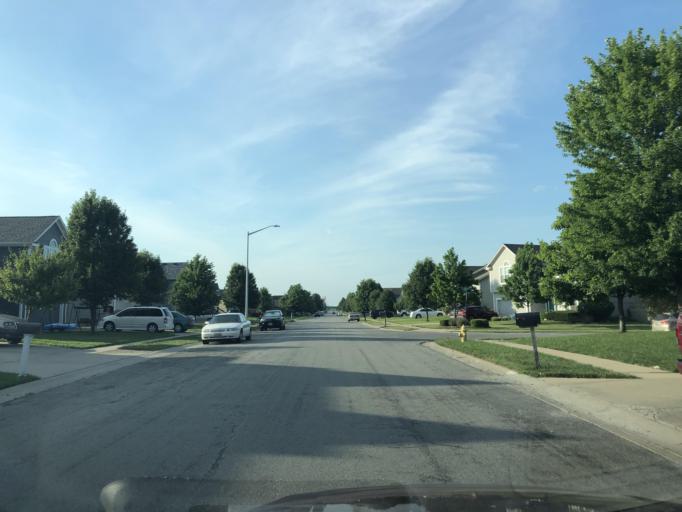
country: US
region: Kansas
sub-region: Johnson County
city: Gardner
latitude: 38.8187
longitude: -94.9362
